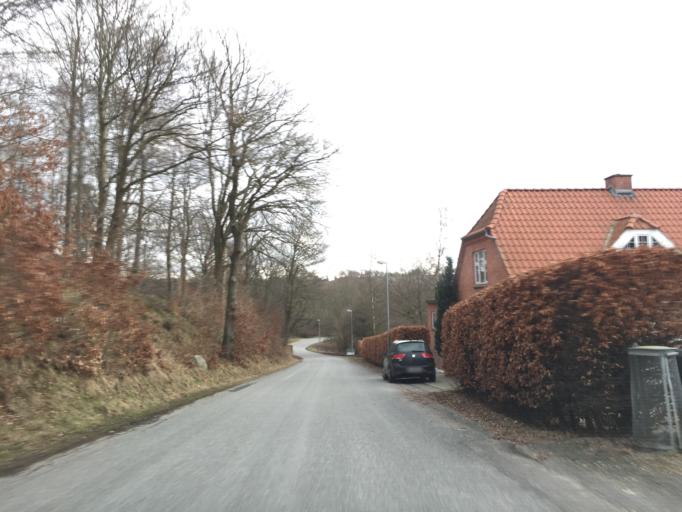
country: DK
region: Central Jutland
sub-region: Viborg Kommune
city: Viborg
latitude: 56.3696
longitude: 9.3215
